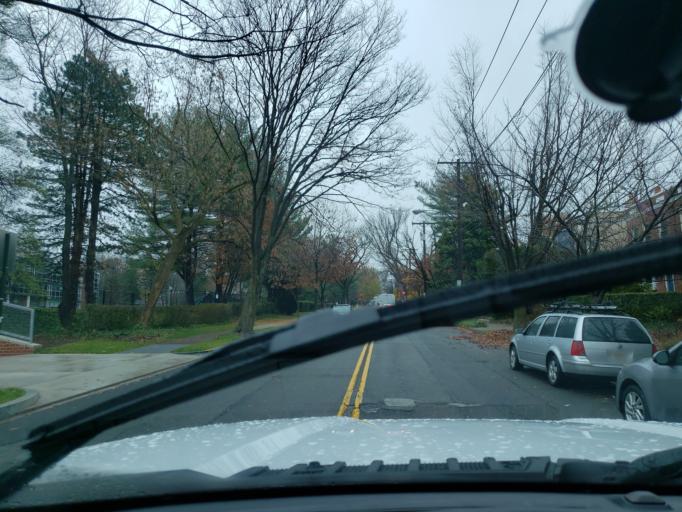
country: US
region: Maryland
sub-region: Montgomery County
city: Friendship Village
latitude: 38.9520
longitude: -77.0849
